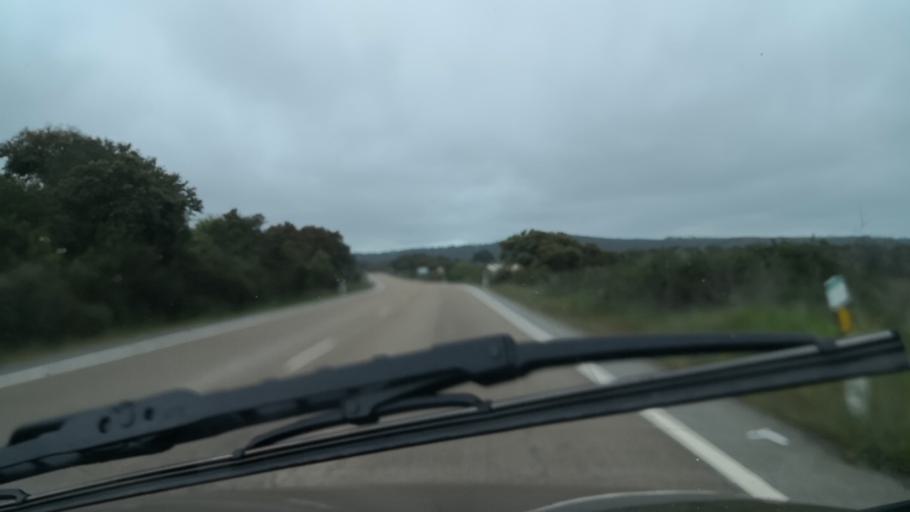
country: ES
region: Extremadura
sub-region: Provincia de Caceres
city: Malpartida de Caceres
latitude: 39.2993
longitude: -6.5173
